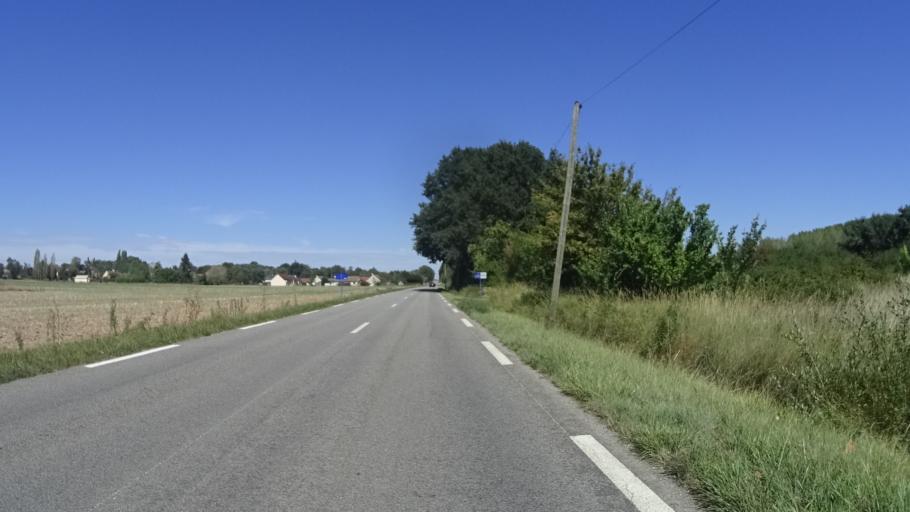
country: FR
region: Centre
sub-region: Departement du Cher
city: Belleville-sur-Loire
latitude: 47.5138
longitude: 2.8459
